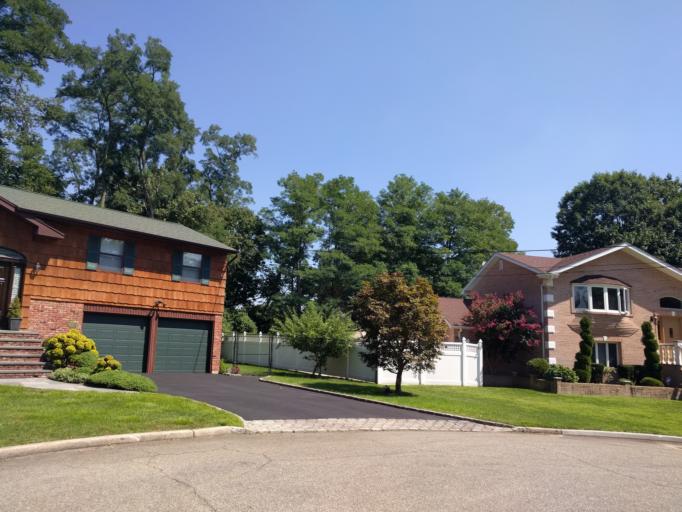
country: US
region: New York
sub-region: Nassau County
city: Locust Valley
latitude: 40.8792
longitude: -73.6184
